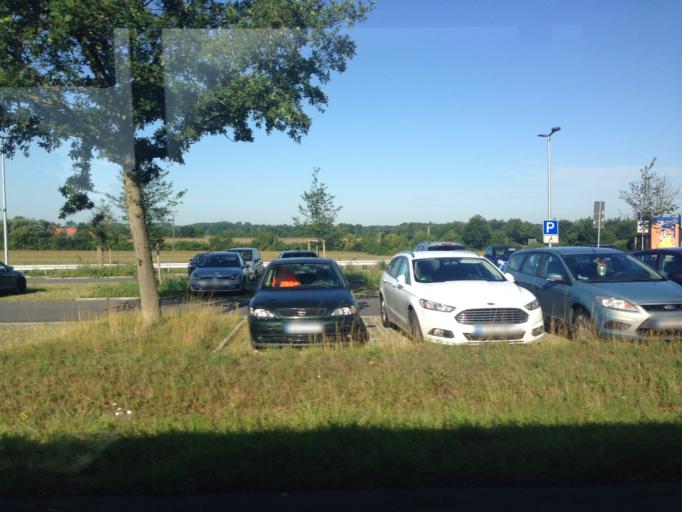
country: DE
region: North Rhine-Westphalia
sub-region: Regierungsbezirk Munster
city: Senden
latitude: 51.9001
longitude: 7.4921
